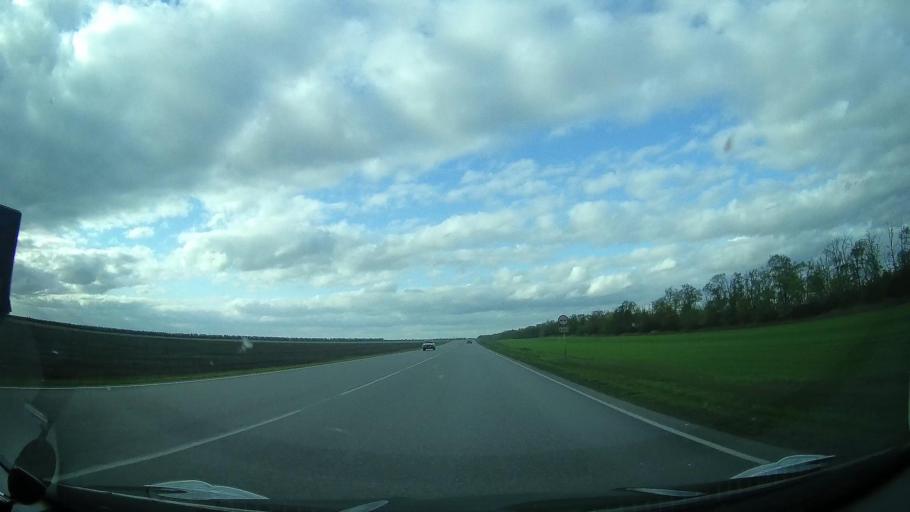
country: RU
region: Rostov
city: Kagal'nitskaya
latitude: 46.8999
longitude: 40.1238
